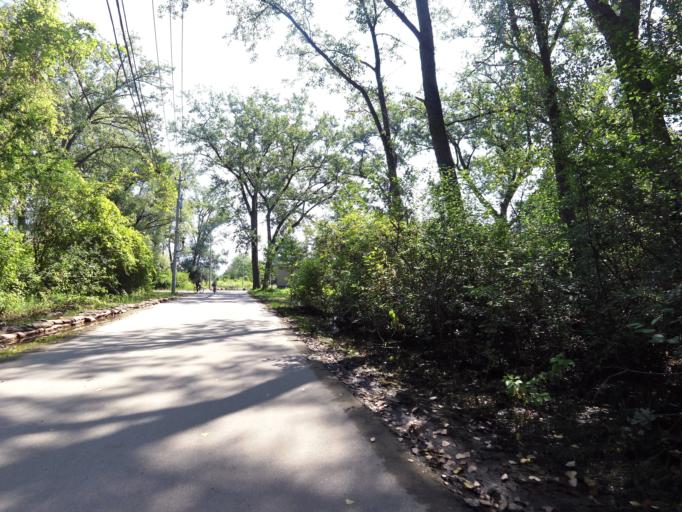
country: CA
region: Ontario
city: Toronto
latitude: 43.6131
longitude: -79.3854
